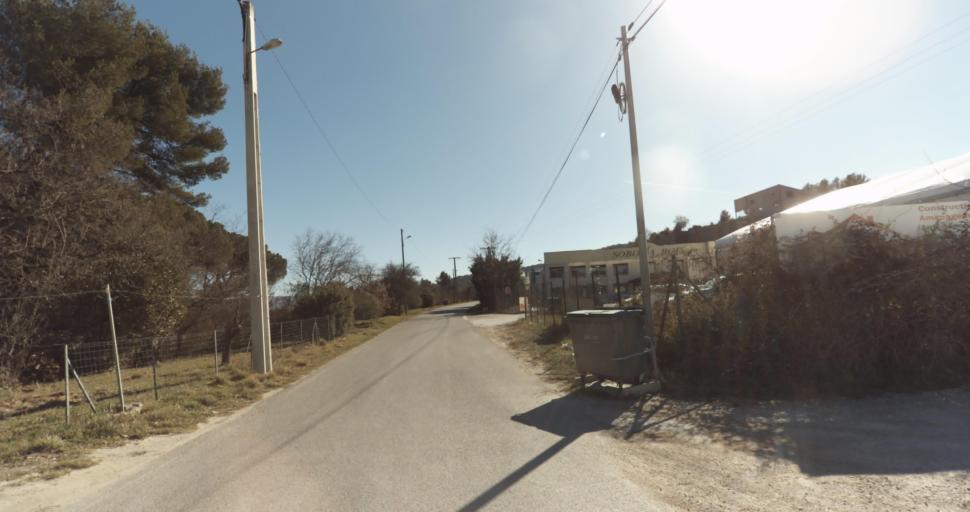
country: FR
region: Provence-Alpes-Cote d'Azur
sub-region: Departement des Bouches-du-Rhone
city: Cadolive
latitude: 43.3991
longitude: 5.5640
